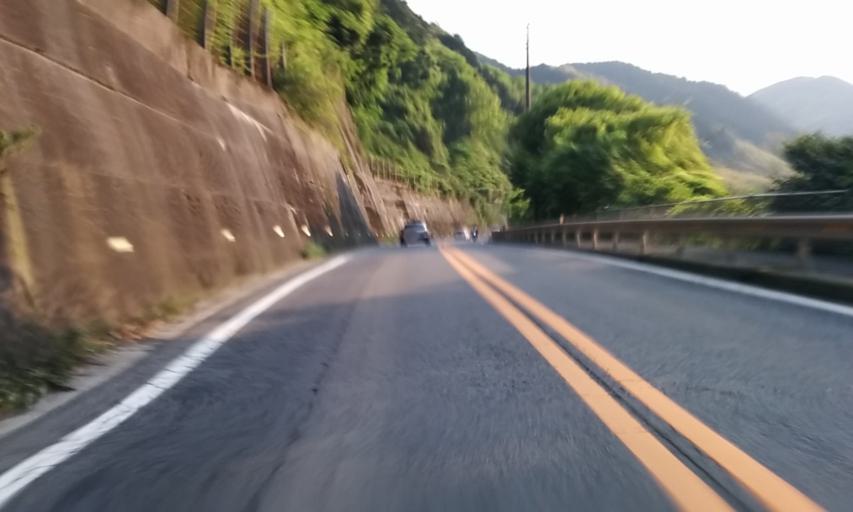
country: JP
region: Ehime
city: Saijo
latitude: 33.8535
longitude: 133.0113
